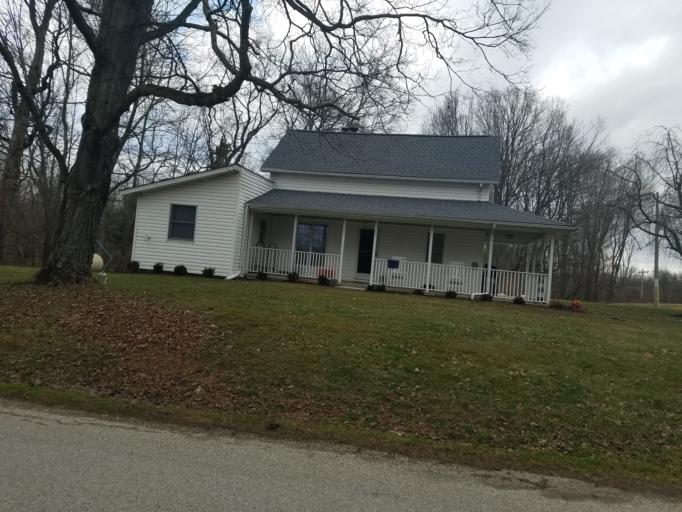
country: US
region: Ohio
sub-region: Morrow County
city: Mount Gilead
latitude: 40.5783
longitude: -82.8080
